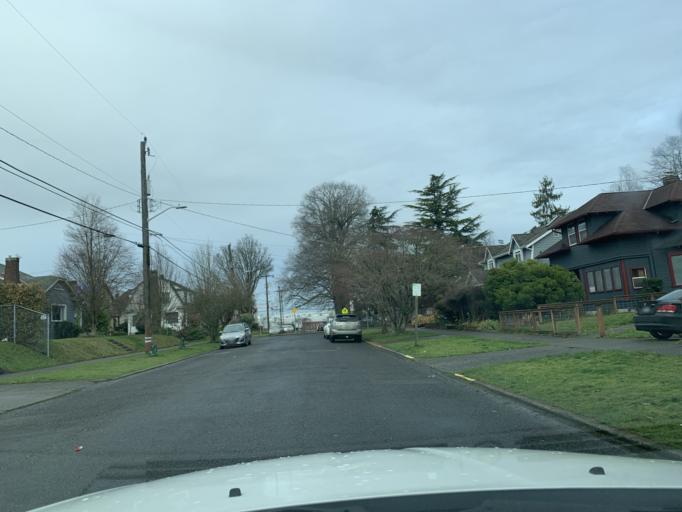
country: US
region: Washington
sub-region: King County
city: Seattle
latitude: 47.6029
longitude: -122.3010
